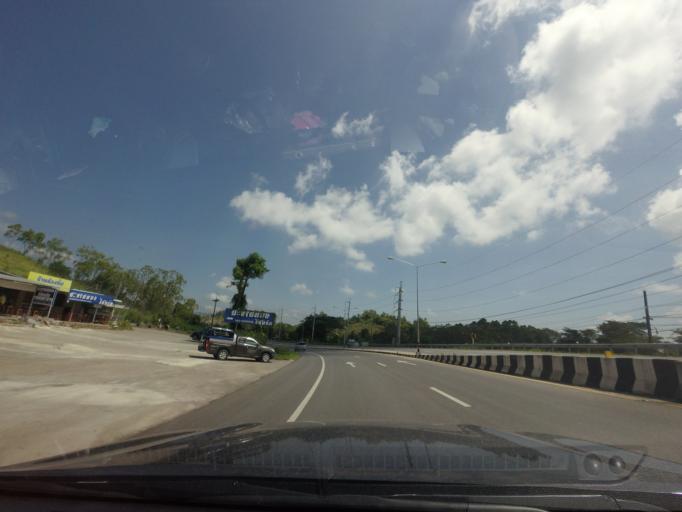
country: TH
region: Phetchabun
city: Khao Kho
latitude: 16.7688
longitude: 101.0536
